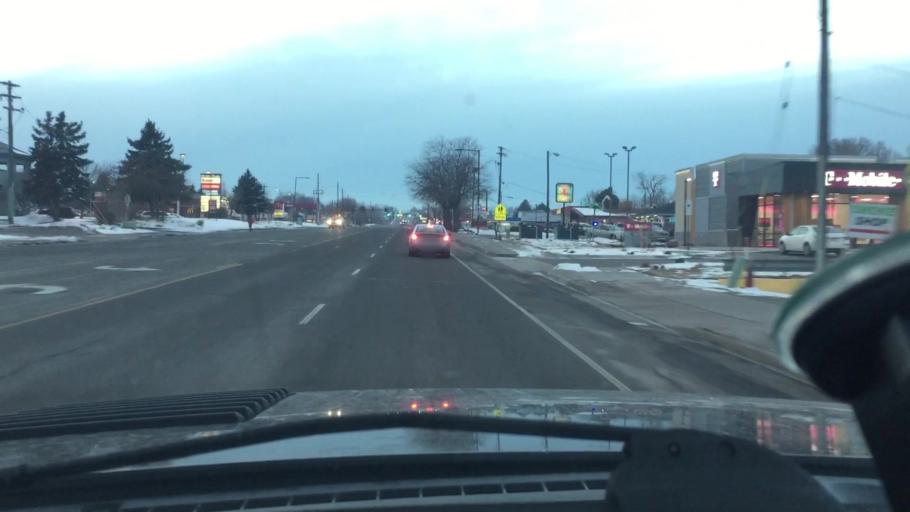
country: US
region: Colorado
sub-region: Adams County
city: Federal Heights
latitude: 39.8491
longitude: -104.9932
